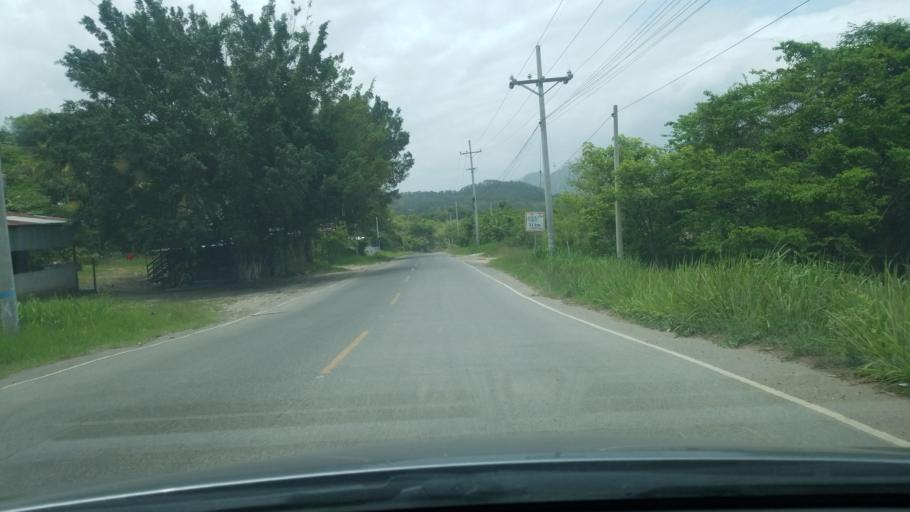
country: HN
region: Copan
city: Santa Rosa de Copan
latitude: 14.7308
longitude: -88.7704
